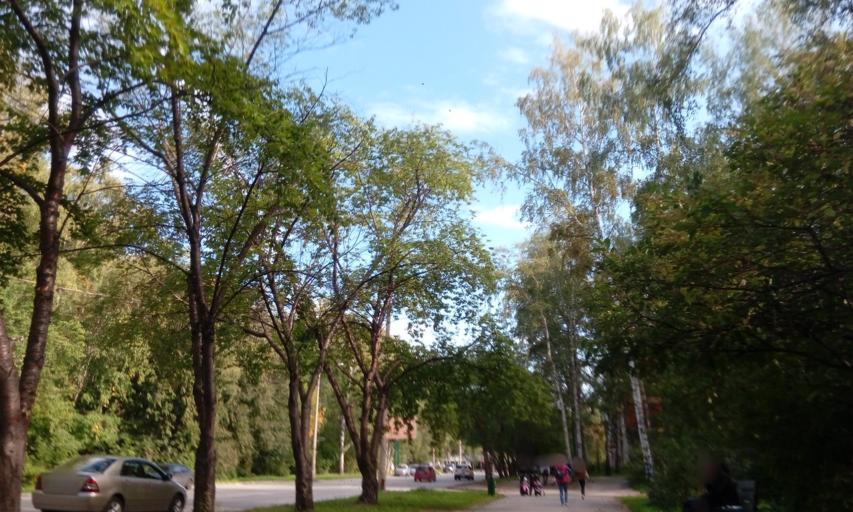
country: RU
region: Novosibirsk
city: Akademgorodok
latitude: 54.8377
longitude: 83.0983
